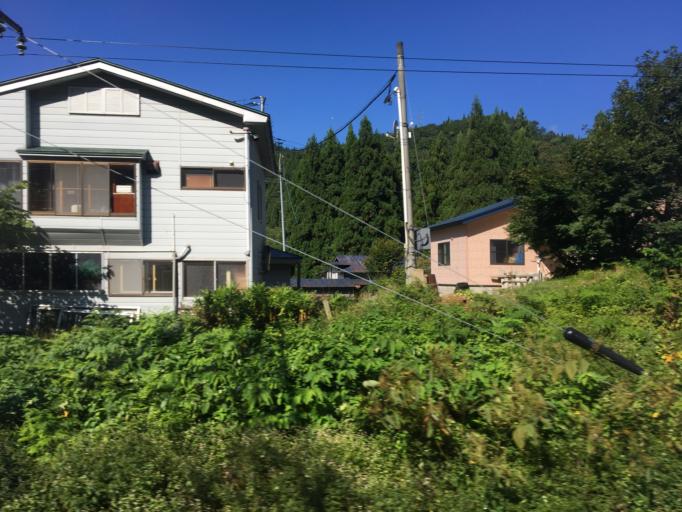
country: JP
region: Akita
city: Odate
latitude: 40.4012
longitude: 140.6088
